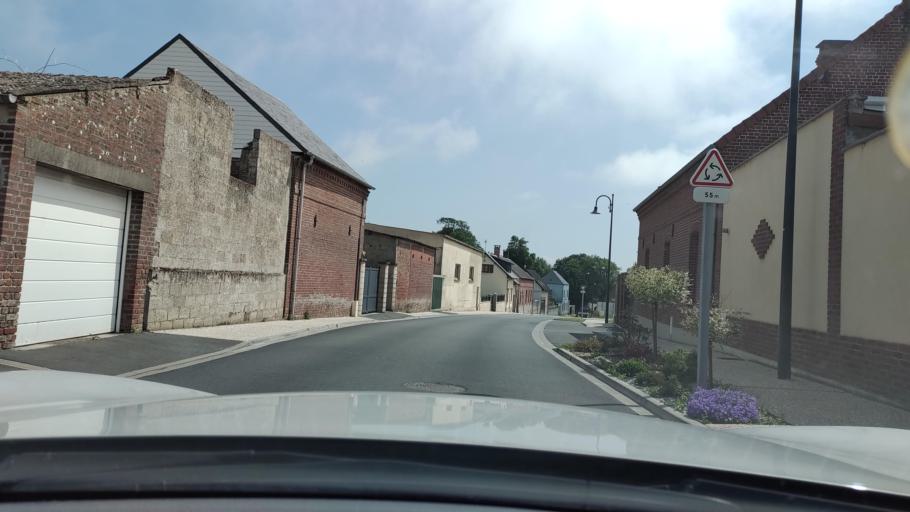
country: FR
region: Picardie
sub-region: Departement de la Somme
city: Ault
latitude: 50.0708
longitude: 1.4604
